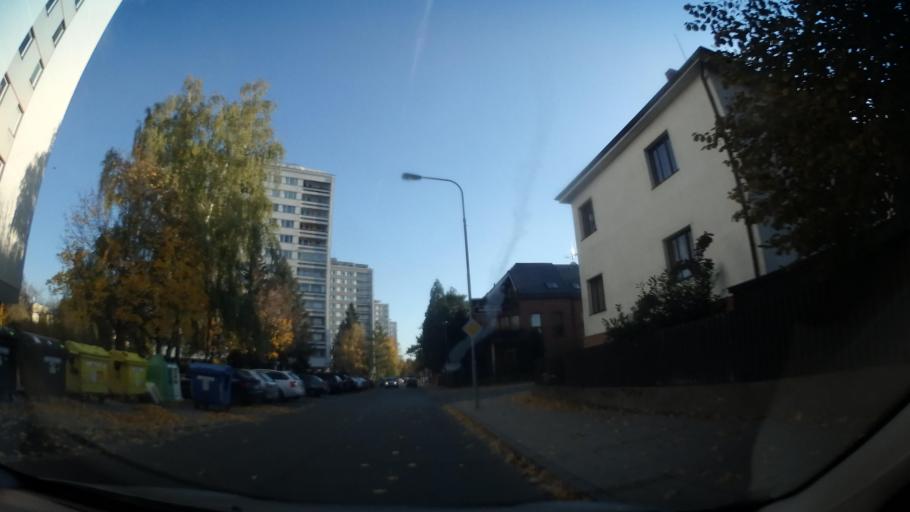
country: CZ
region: Kralovehradecky
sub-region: Okres Hradec Kralove
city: Hradec Kralove
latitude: 50.2056
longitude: 15.8185
